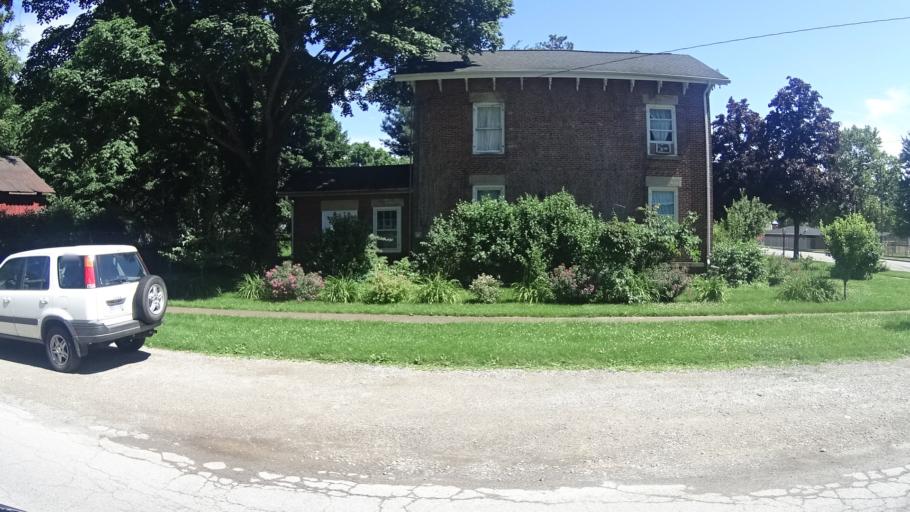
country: US
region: Ohio
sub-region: Erie County
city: Milan
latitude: 41.2939
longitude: -82.6024
